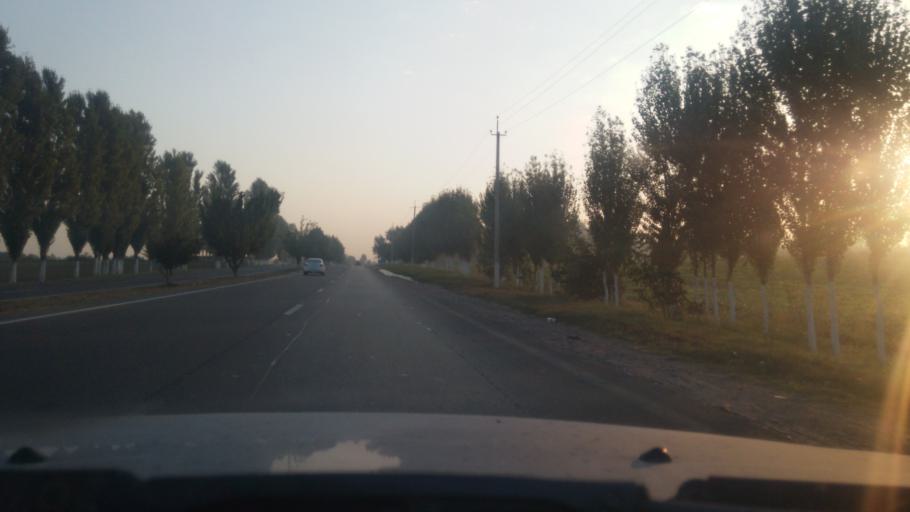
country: UZ
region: Toshkent
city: Yangiyul
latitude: 41.1557
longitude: 69.0441
